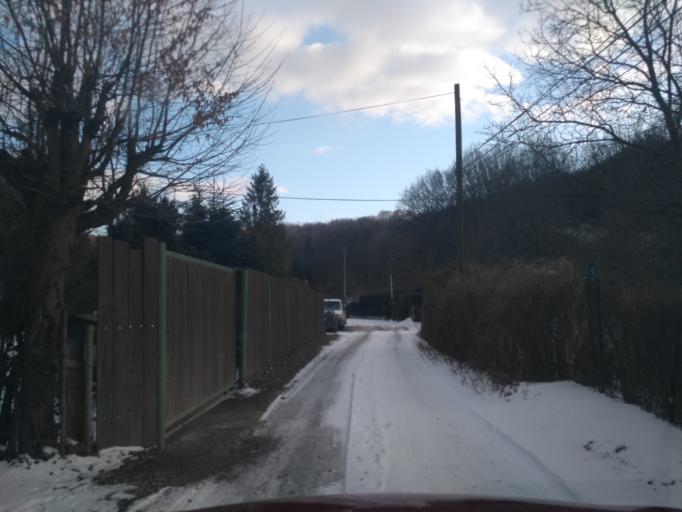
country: SK
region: Kosicky
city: Kosice
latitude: 48.7290
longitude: 21.1627
